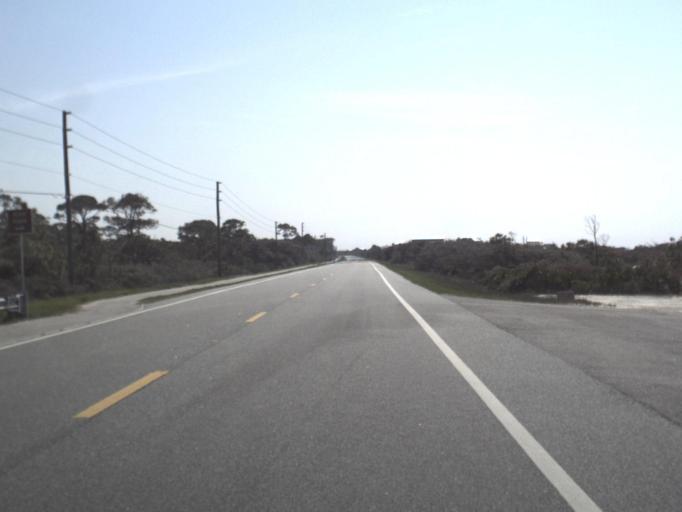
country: US
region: Florida
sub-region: Gulf County
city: Port Saint Joe
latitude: 29.7275
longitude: -85.3894
